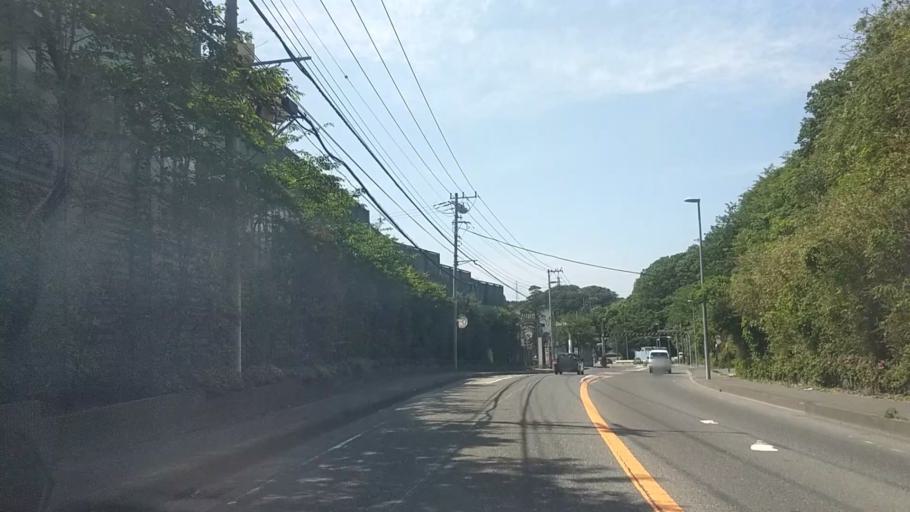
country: JP
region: Kanagawa
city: Kamakura
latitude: 35.3391
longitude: 139.5845
